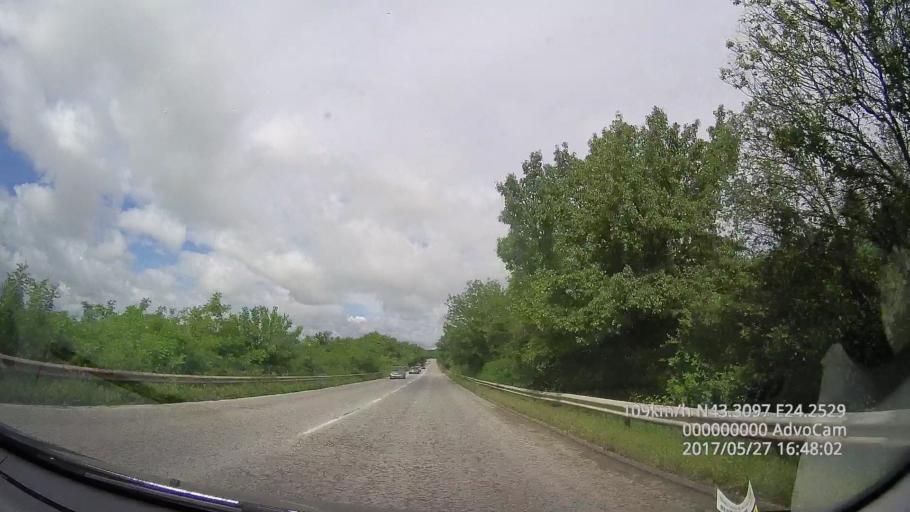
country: BG
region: Pleven
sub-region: Obshtina Cherven Bryag
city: Koynare
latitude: 43.3102
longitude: 24.2537
